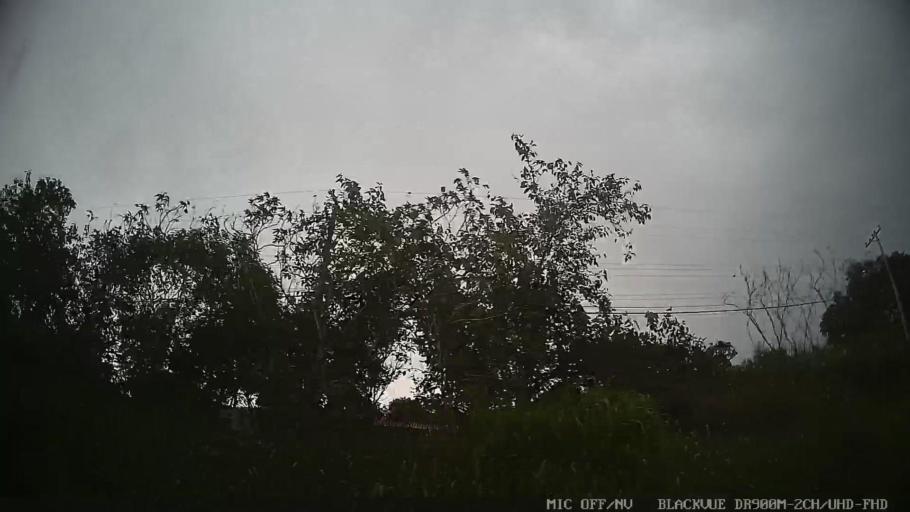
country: BR
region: Sao Paulo
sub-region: Pedreira
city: Pedreira
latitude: -22.7246
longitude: -46.8542
